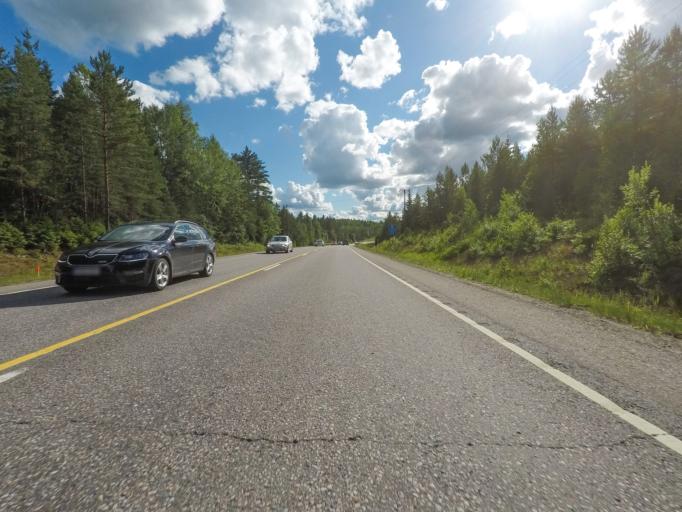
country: FI
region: Uusimaa
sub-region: Helsinki
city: Nurmijaervi
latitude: 60.5239
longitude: 24.6658
